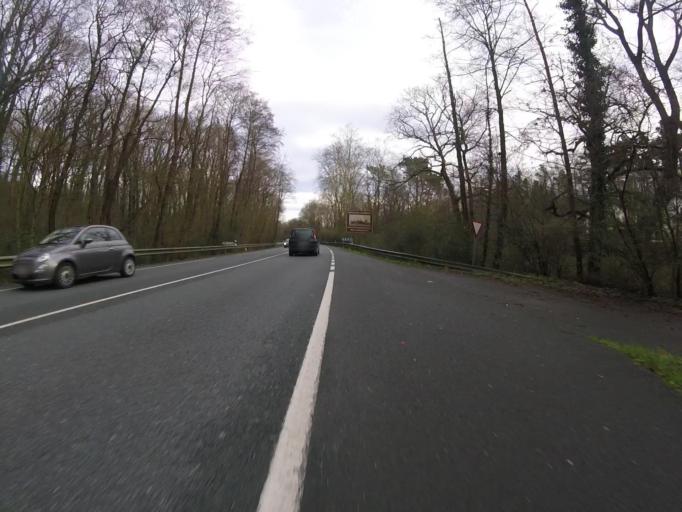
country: ES
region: Basque Country
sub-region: Provincia de Guipuzcoa
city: Irun
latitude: 43.3328
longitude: -1.8228
